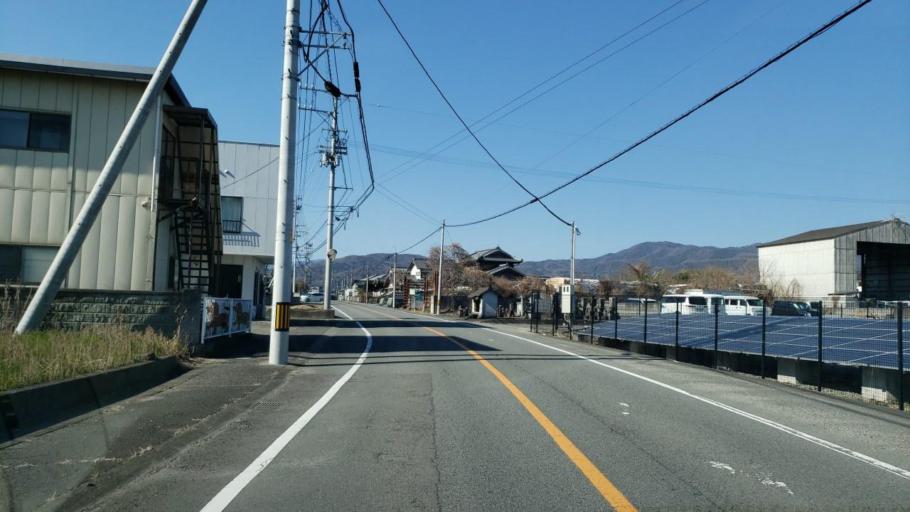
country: JP
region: Tokushima
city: Kamojimacho-jogejima
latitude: 34.0973
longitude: 134.3407
